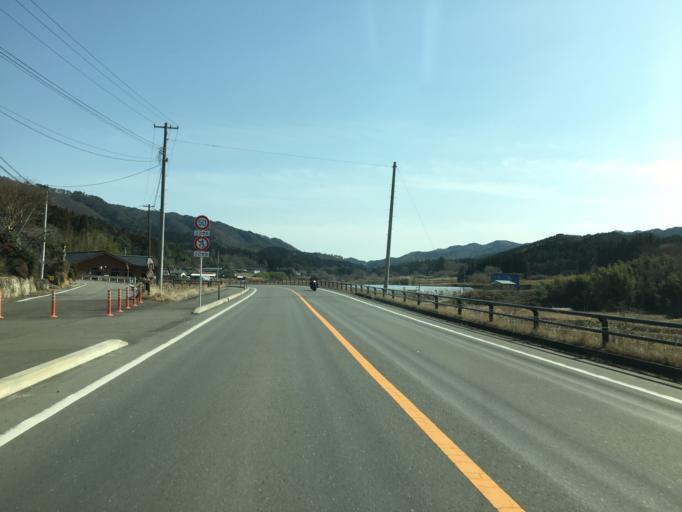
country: JP
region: Ibaraki
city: Daigo
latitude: 36.8350
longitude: 140.4506
